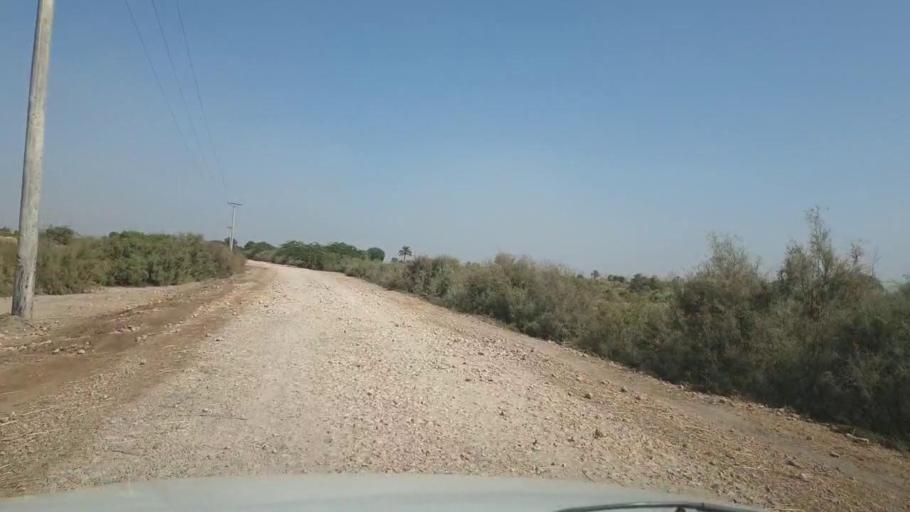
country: PK
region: Sindh
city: Mirpur Sakro
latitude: 24.4020
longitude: 67.7623
